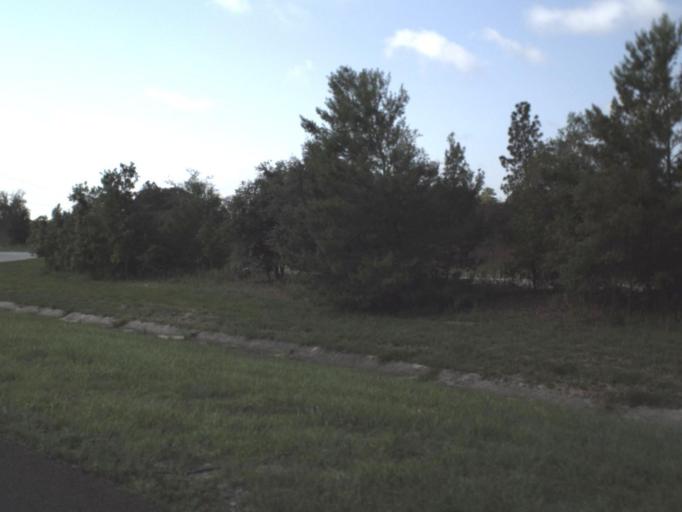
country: US
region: Florida
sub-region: Citrus County
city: Sugarmill Woods
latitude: 28.6908
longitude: -82.5027
